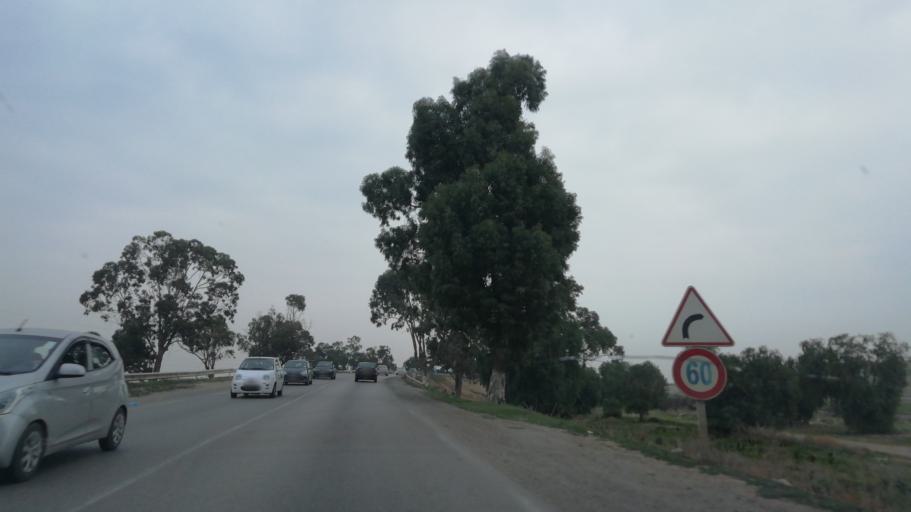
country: DZ
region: Mascara
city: Sig
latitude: 35.5536
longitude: -0.2638
